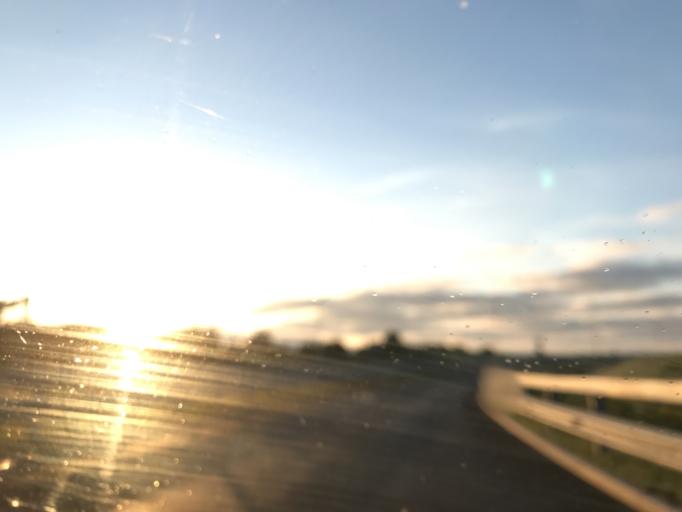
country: RU
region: Kaliningrad
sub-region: Gorod Kaliningrad
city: Pionerskiy
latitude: 54.9096
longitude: 20.2011
